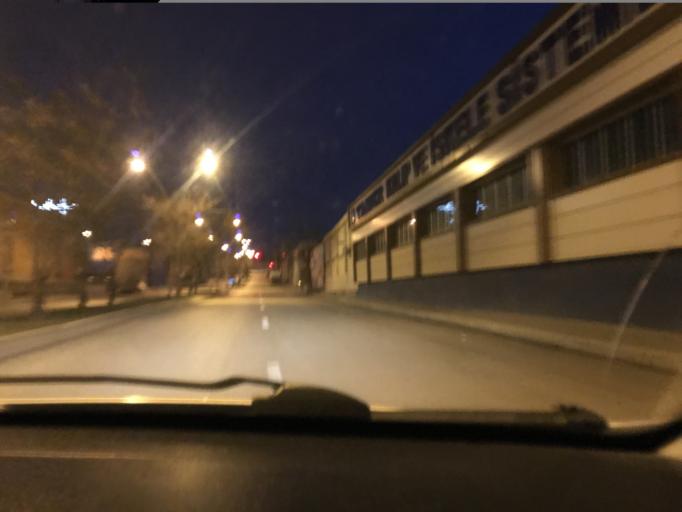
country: TR
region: Ankara
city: Batikent
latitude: 39.9721
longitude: 32.7401
